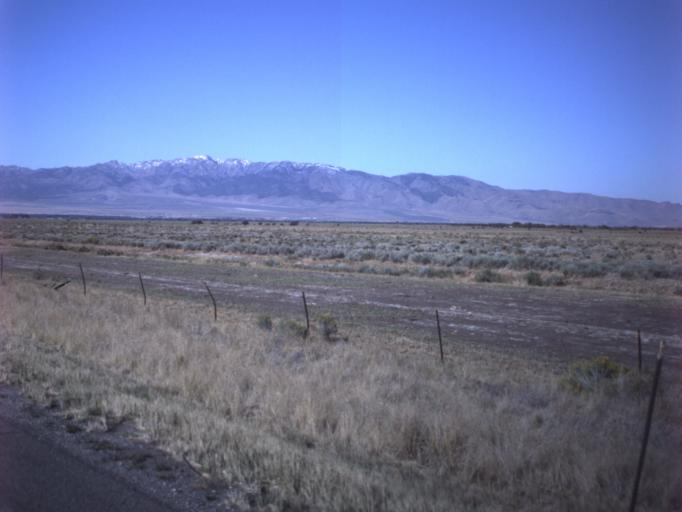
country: US
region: Utah
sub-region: Tooele County
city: Erda
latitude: 40.6155
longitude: -112.3690
